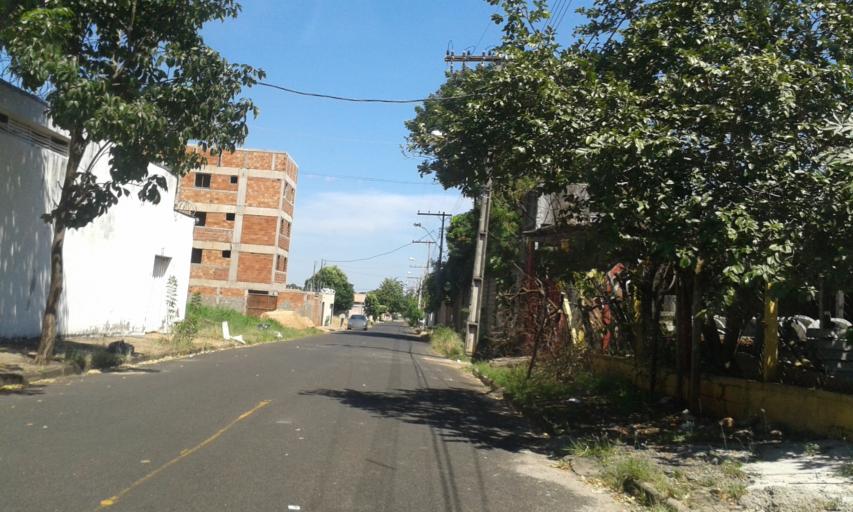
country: BR
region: Minas Gerais
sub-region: Uberlandia
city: Uberlandia
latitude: -18.9291
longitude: -48.2477
